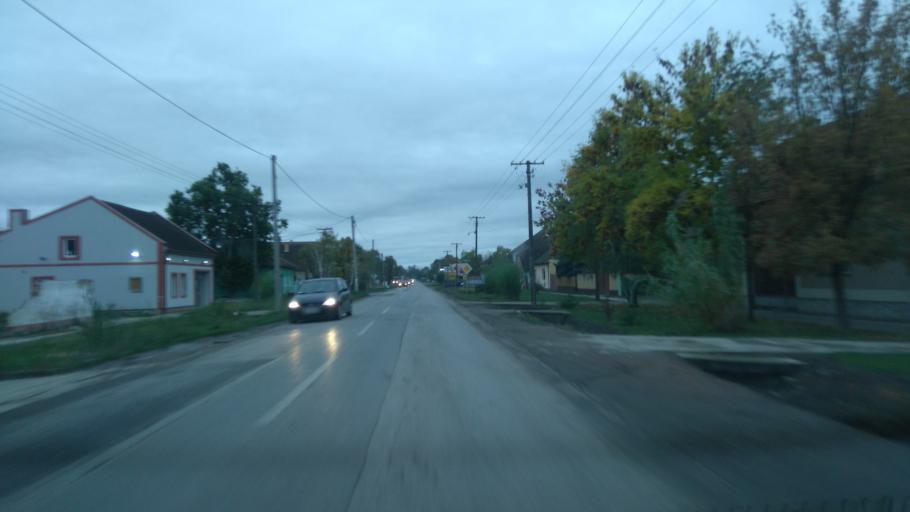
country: RS
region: Autonomna Pokrajina Vojvodina
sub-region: Juznobacki Okrug
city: Zabalj
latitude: 45.3658
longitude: 20.0653
